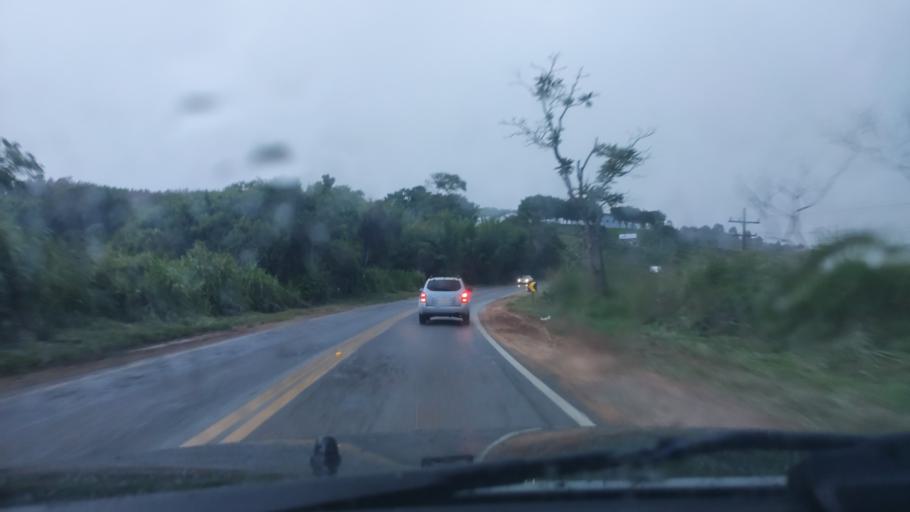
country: BR
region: Sao Paulo
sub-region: Braganca Paulista
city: Braganca Paulista
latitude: -22.8051
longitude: -46.5538
